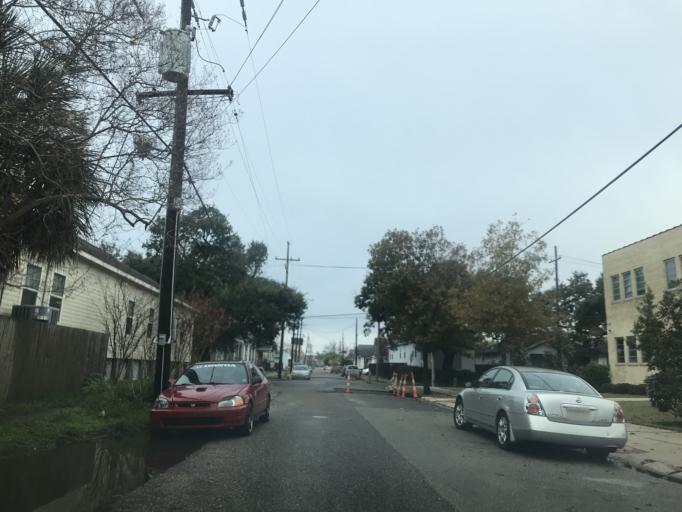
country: US
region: Louisiana
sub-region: Orleans Parish
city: New Orleans
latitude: 29.9723
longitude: -90.1076
